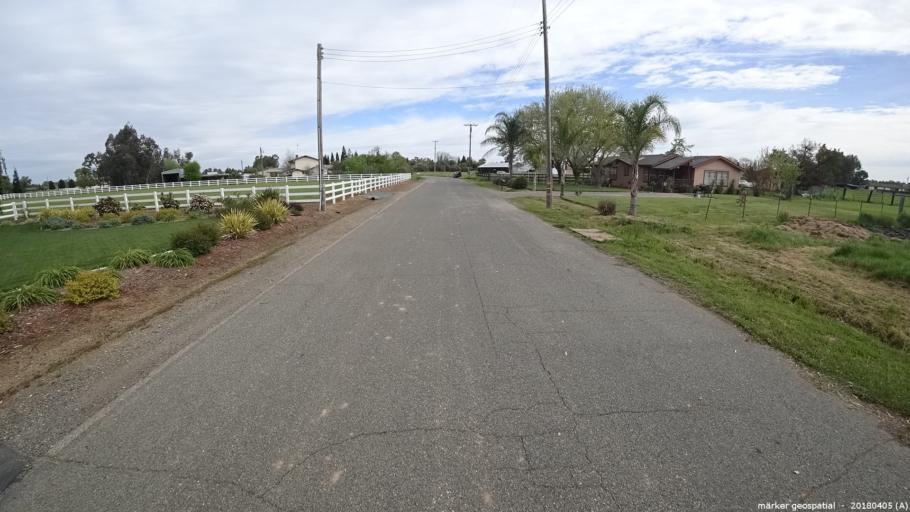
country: US
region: California
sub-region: Sacramento County
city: Galt
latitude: 38.2649
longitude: -121.3296
